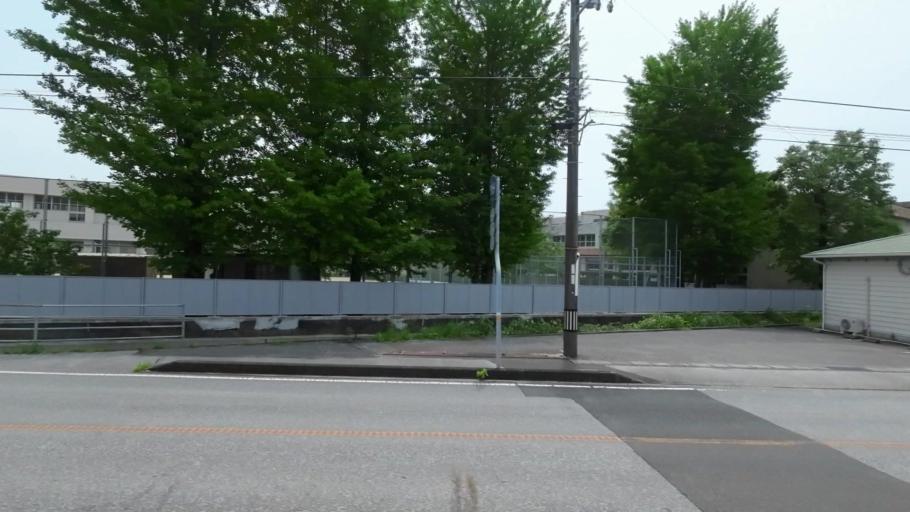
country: JP
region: Kochi
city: Kochi-shi
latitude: 33.5811
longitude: 133.6496
